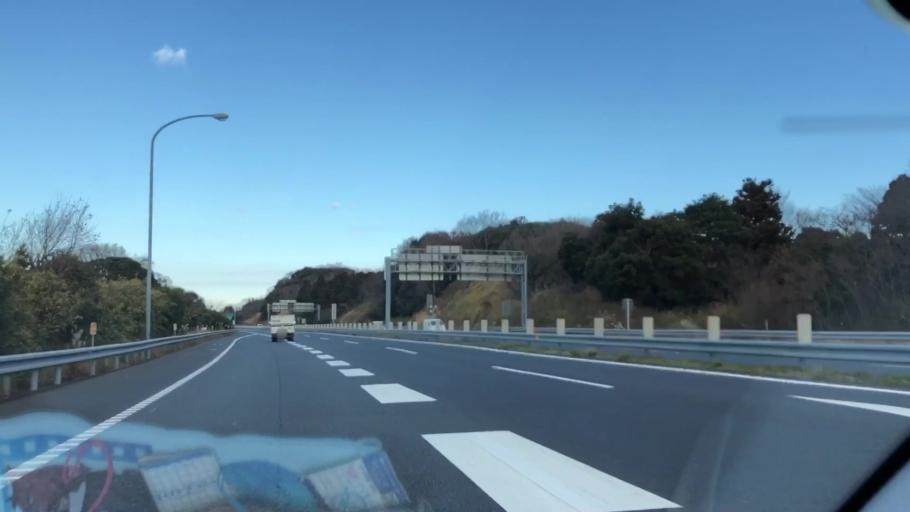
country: JP
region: Chiba
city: Kisarazu
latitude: 35.3811
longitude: 139.9774
